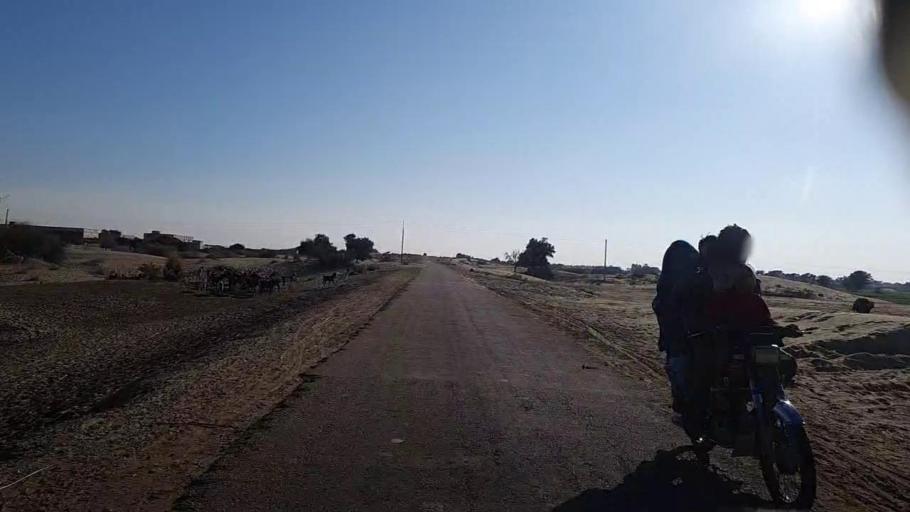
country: PK
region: Sindh
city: Khairpur
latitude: 27.9054
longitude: 69.7498
